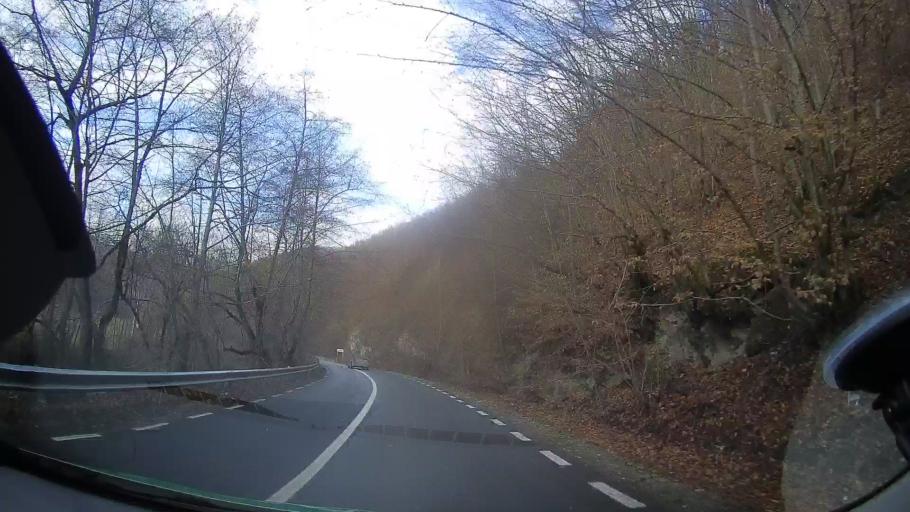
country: RO
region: Cluj
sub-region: Comuna Baisoara
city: Baisoara
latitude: 46.6082
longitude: 23.4187
